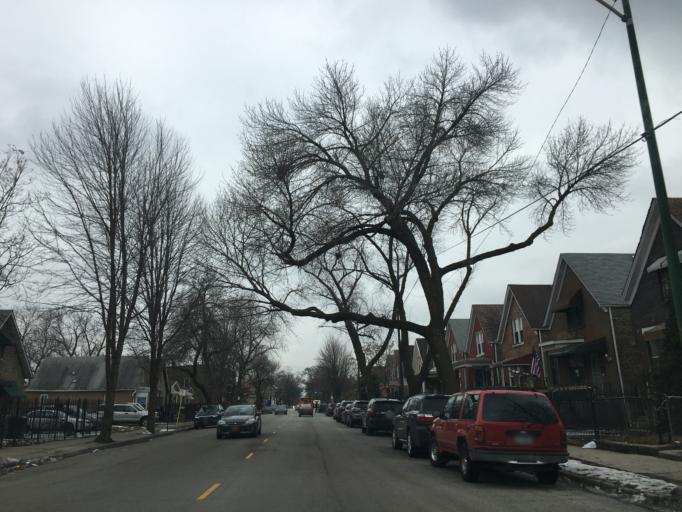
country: US
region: Illinois
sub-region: Cook County
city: Cicero
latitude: 41.8974
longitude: -87.7115
